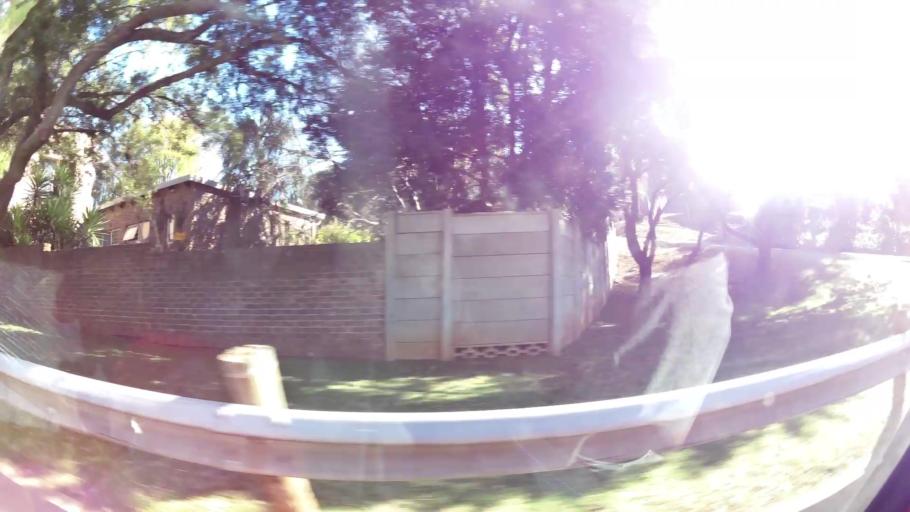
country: ZA
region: Gauteng
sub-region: City of Johannesburg Metropolitan Municipality
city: Roodepoort
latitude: -26.1204
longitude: 27.8663
